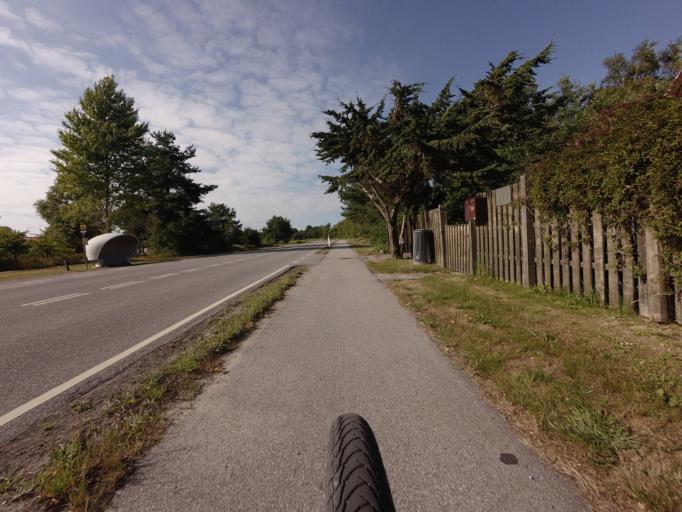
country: DK
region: North Denmark
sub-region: Laeso Kommune
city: Byrum
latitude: 57.2793
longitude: 10.9359
